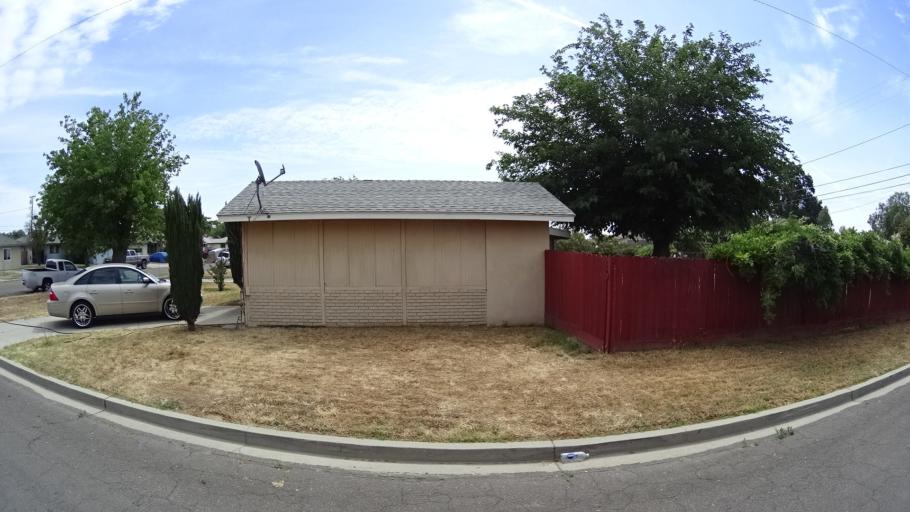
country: US
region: California
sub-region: Kings County
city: Hanford
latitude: 36.3473
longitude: -119.6450
